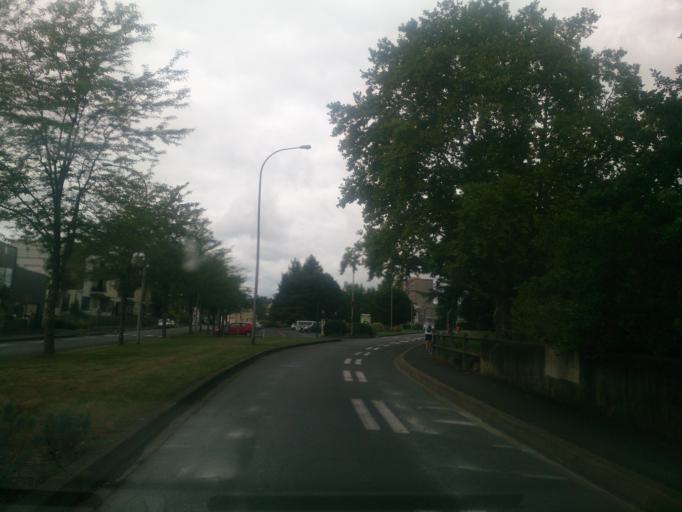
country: FR
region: Limousin
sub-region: Departement de la Correze
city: Brive-la-Gaillarde
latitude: 45.1628
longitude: 1.5432
